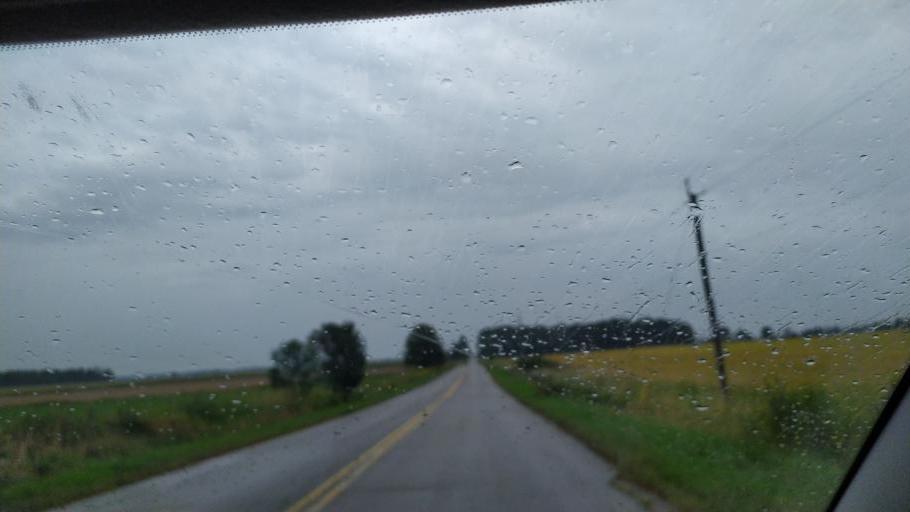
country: CA
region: Ontario
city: Kitchener
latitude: 43.3288
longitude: -80.6713
